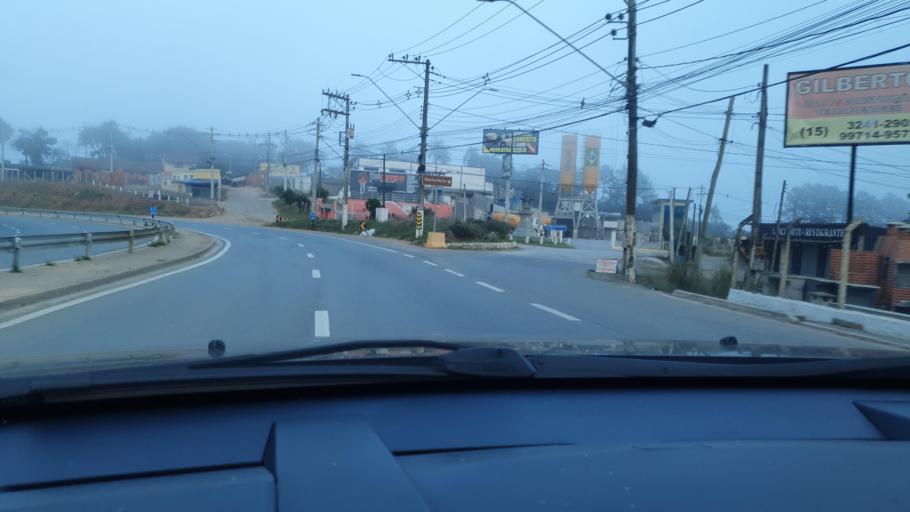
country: BR
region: Sao Paulo
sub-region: Ibiuna
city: Ibiuna
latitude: -23.6559
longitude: -47.1870
